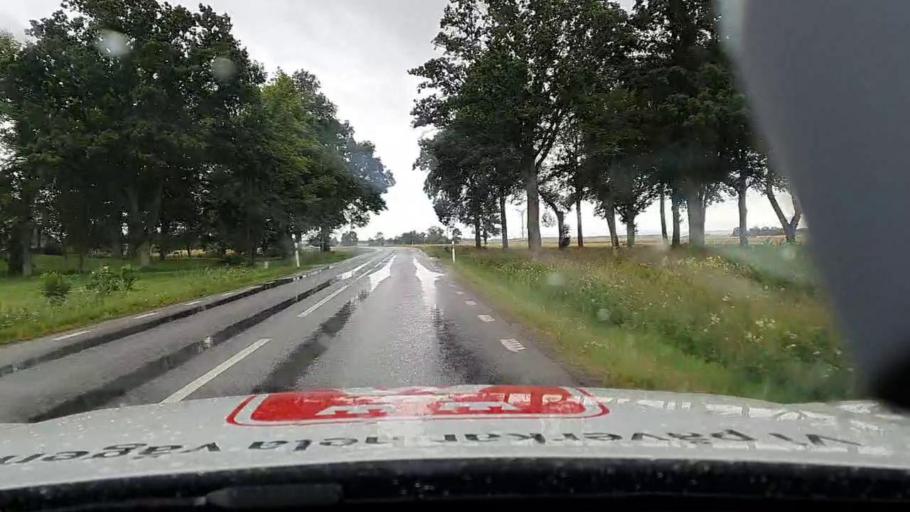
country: SE
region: Vaestra Goetaland
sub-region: Toreboda Kommun
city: Toereboda
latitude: 58.6182
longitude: 14.0124
